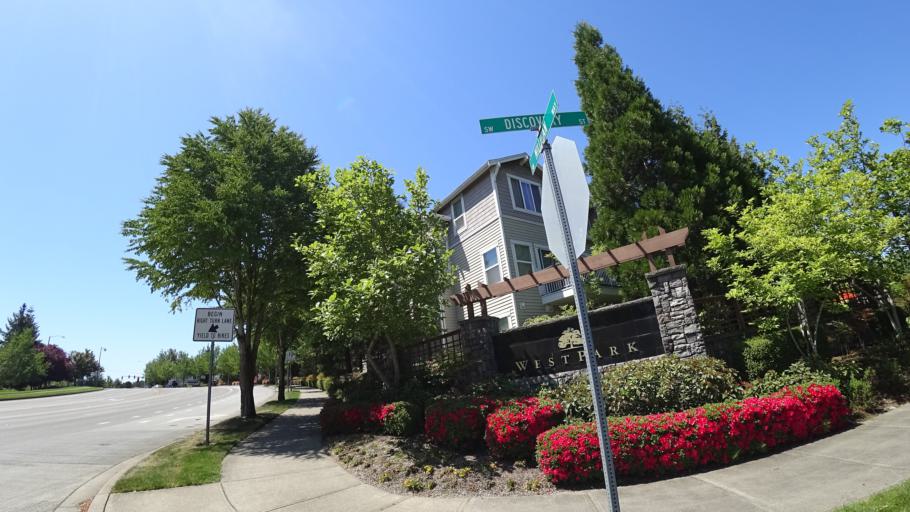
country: US
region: Oregon
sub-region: Washington County
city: Aloha
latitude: 45.4931
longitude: -122.8414
